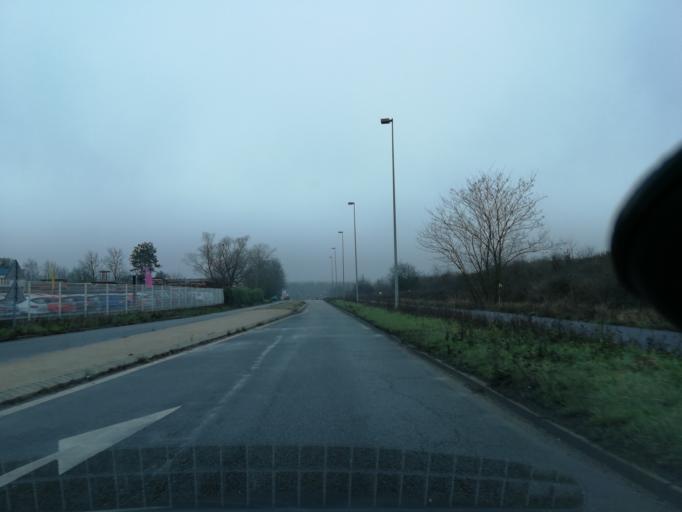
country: FR
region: Ile-de-France
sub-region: Departement des Yvelines
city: Buc
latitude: 48.7620
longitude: 2.1256
